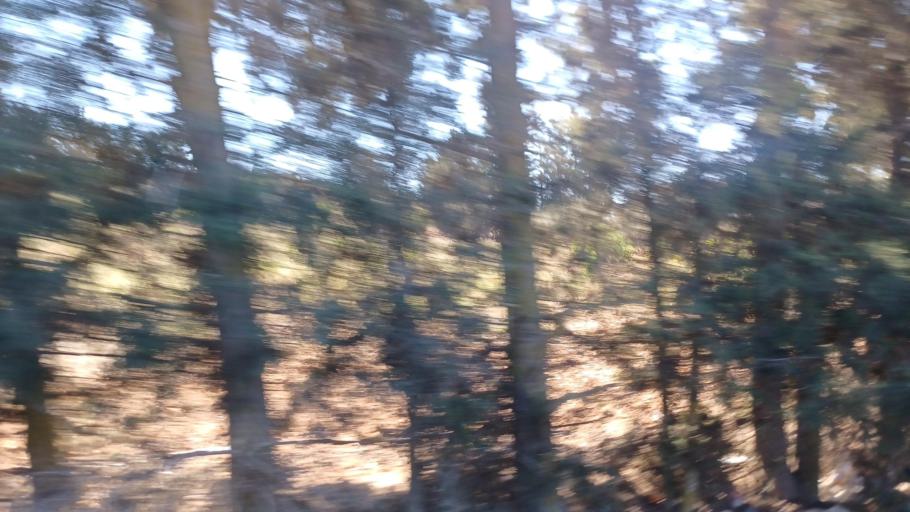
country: CY
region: Pafos
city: Mesogi
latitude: 34.8143
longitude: 32.4779
